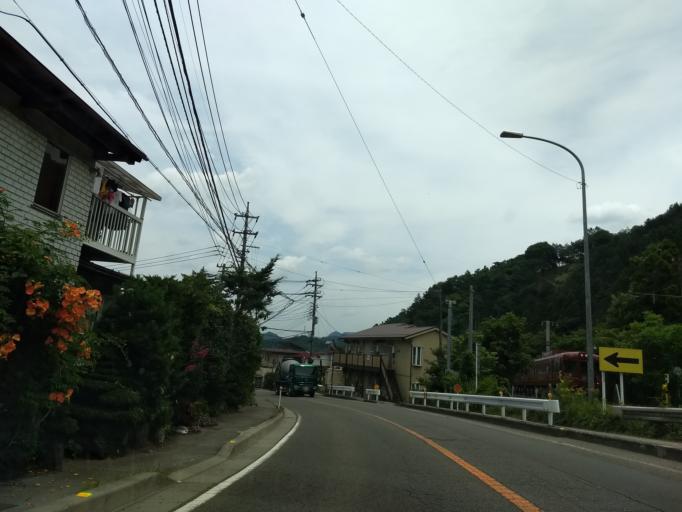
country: JP
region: Yamanashi
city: Otsuki
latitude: 35.5388
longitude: 138.8851
